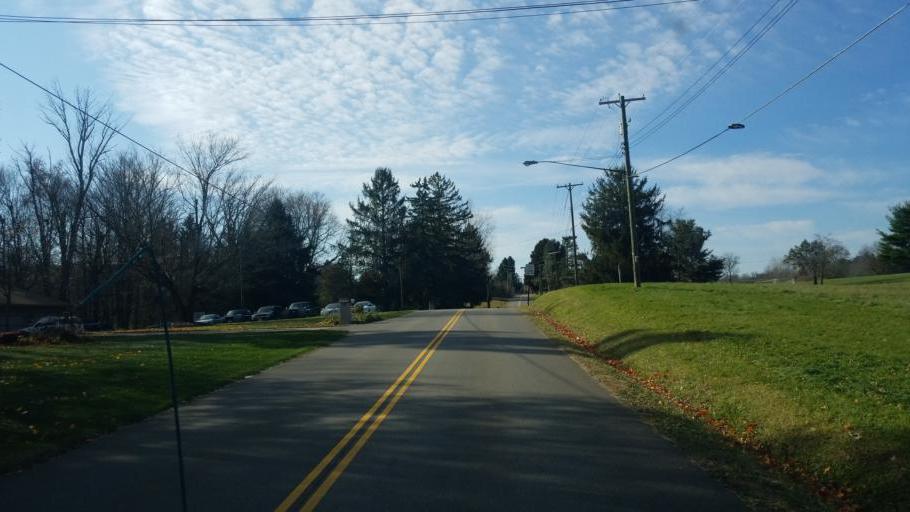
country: US
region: Ohio
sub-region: Richland County
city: Mansfield
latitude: 40.7211
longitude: -82.5205
